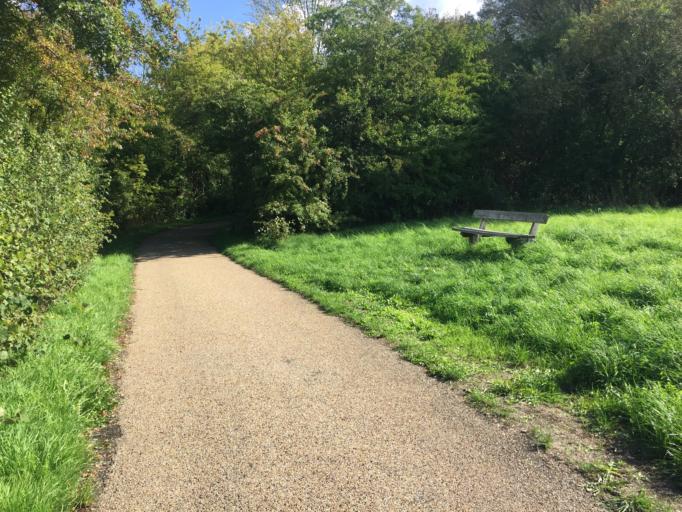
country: DK
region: Capital Region
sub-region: Herlev Kommune
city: Herlev
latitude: 55.7481
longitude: 12.4427
